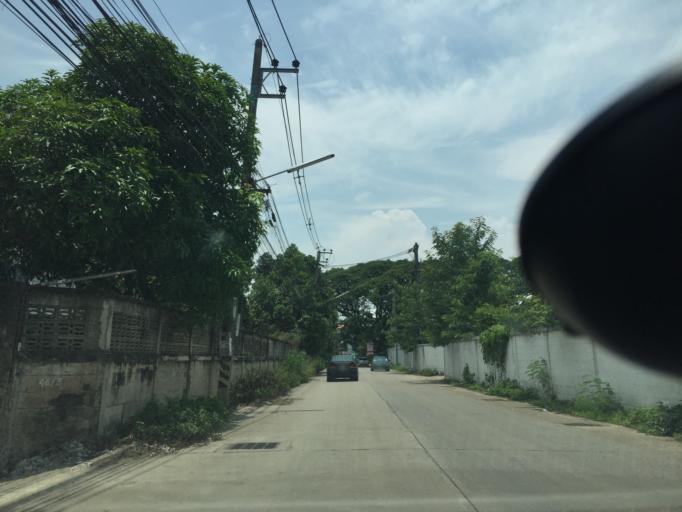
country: TH
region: Chiang Mai
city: Chiang Mai
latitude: 18.8081
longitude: 98.9751
